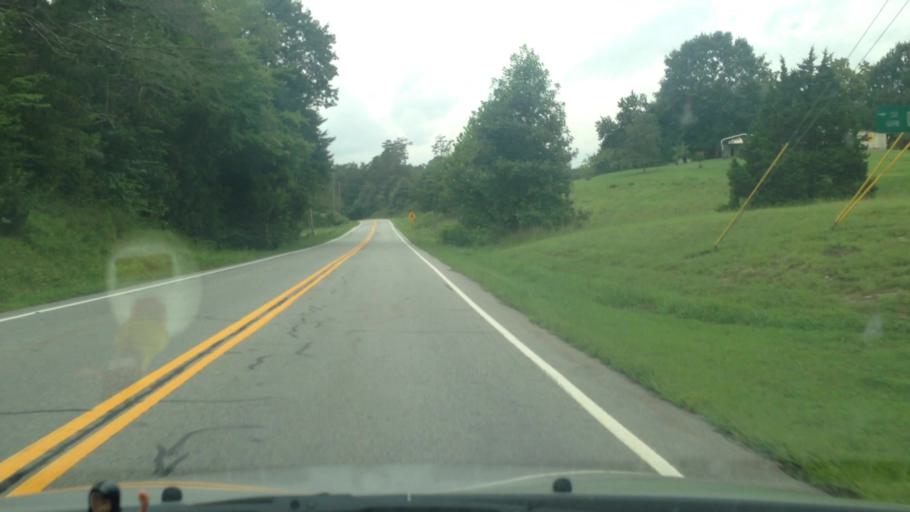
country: US
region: North Carolina
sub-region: Stokes County
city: Danbury
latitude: 36.4061
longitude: -80.1282
